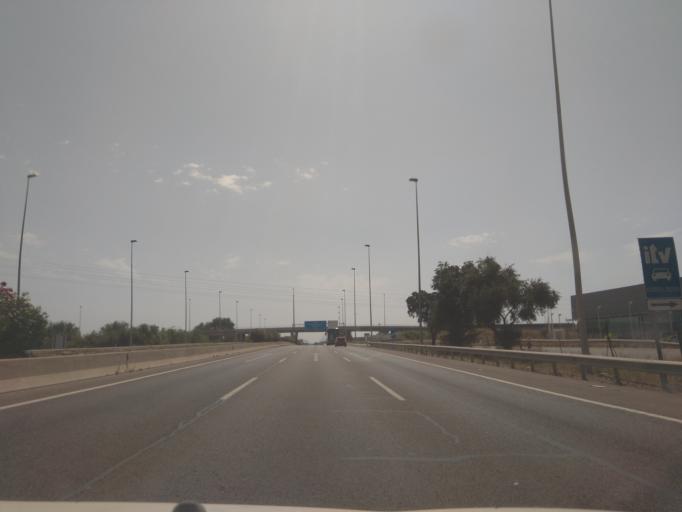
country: ES
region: Valencia
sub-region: Provincia de Valencia
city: Alfafar
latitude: 39.4029
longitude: -0.3854
